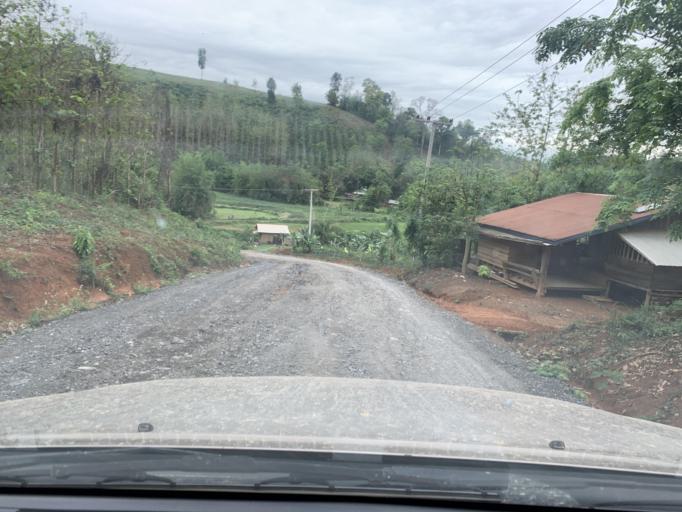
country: TH
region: Nan
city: Mae Charim
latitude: 18.4183
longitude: 101.4646
